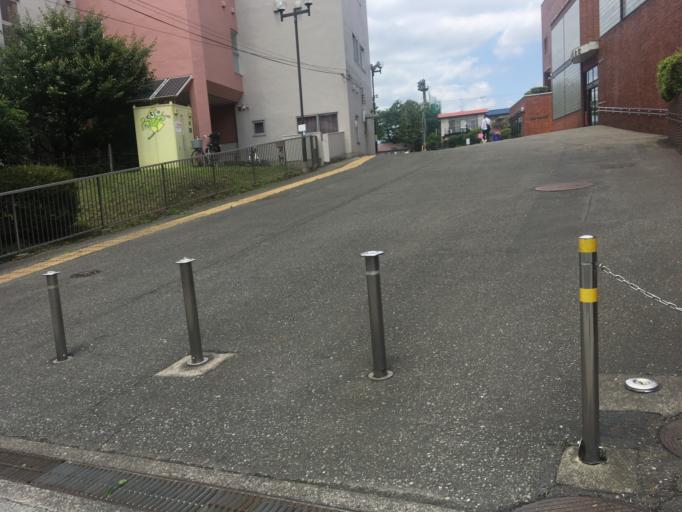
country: JP
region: Tokyo
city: Fussa
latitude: 35.7336
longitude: 139.3375
